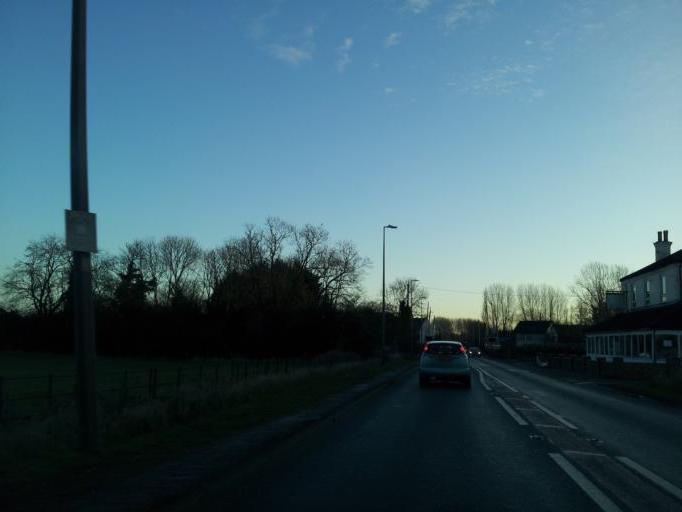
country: GB
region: England
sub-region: Lincolnshire
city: Sudbrooke
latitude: 53.2699
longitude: -0.4251
